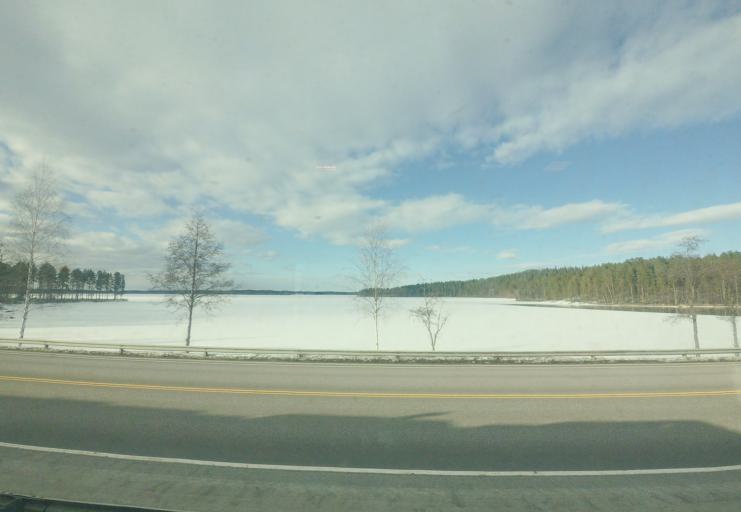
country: FI
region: Southern Savonia
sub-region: Savonlinna
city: Punkaharju
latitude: 61.8029
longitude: 29.2965
